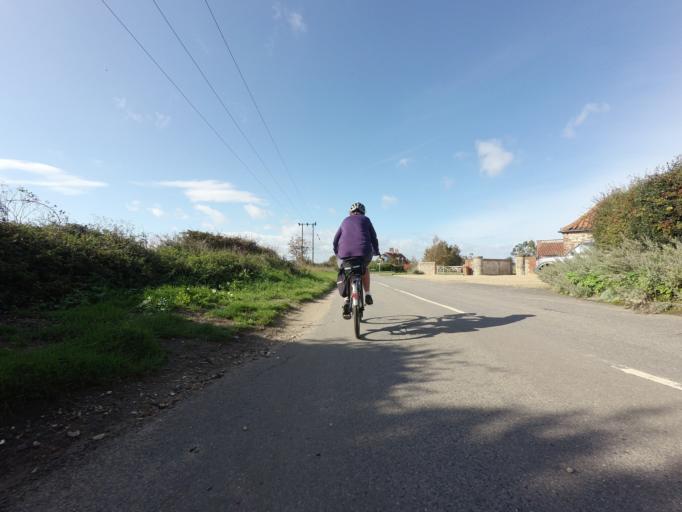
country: GB
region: England
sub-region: Norfolk
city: Hunstanton
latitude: 52.9358
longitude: 0.6088
